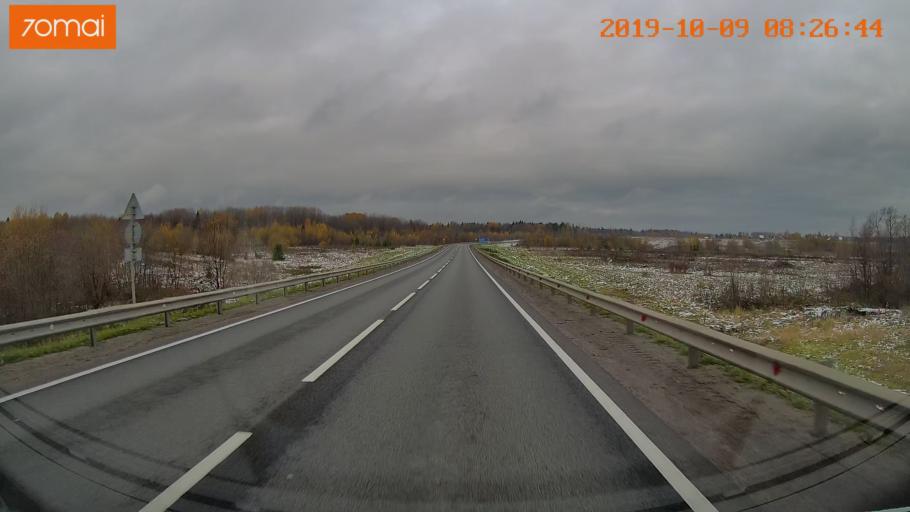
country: RU
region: Vologda
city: Gryazovets
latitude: 58.7962
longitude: 40.2614
